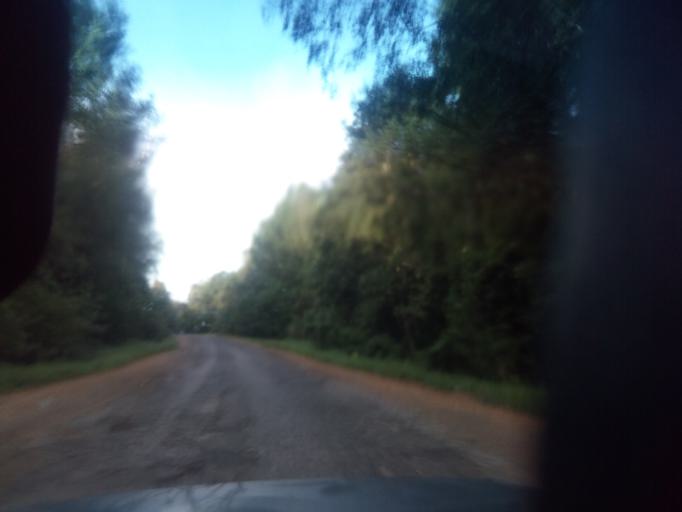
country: BY
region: Vitebsk
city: Dzisna
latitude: 55.6275
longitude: 28.2971
